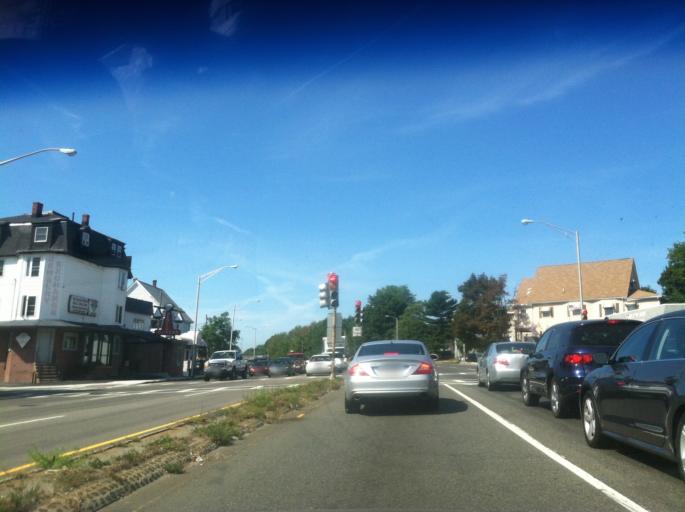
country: US
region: Massachusetts
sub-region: Suffolk County
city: Chelsea
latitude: 42.3860
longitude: -71.0296
